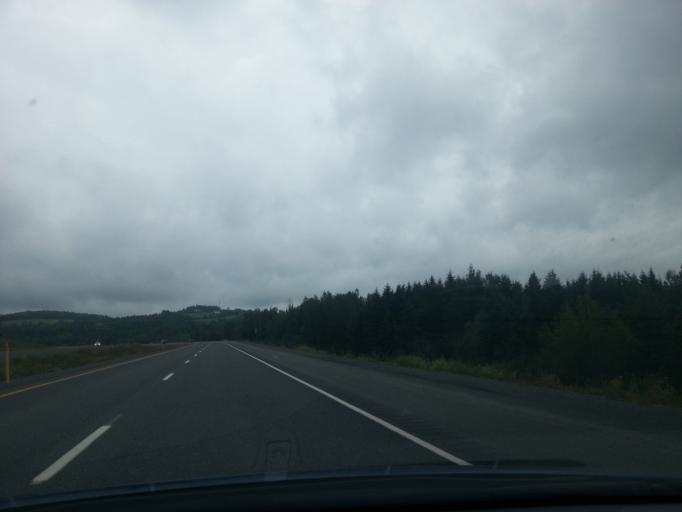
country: CA
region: New Brunswick
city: Florenceville-Bristol
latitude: 46.5111
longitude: -67.6989
